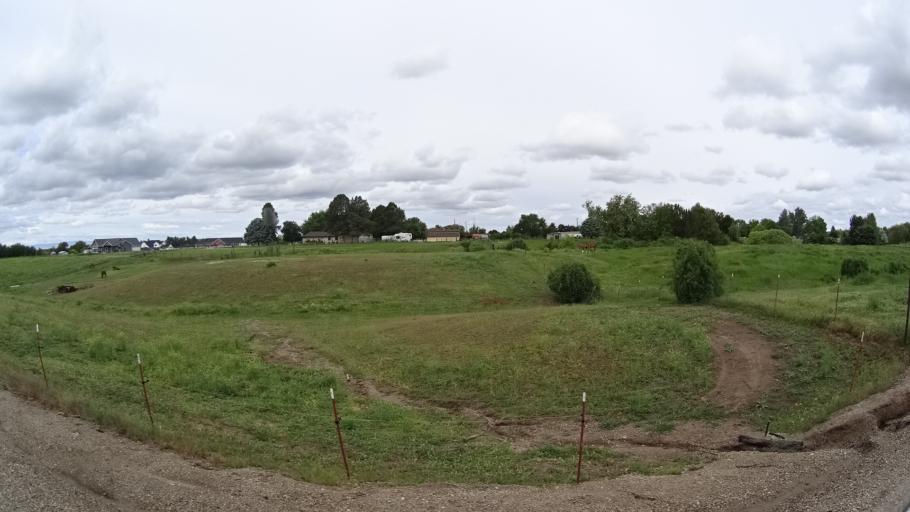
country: US
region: Idaho
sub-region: Ada County
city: Eagle
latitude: 43.7251
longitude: -116.3541
